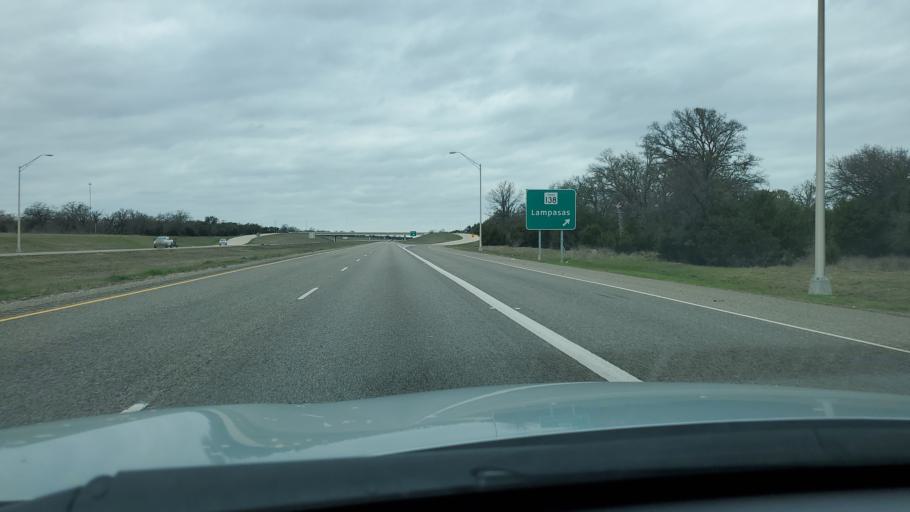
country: US
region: Texas
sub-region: Williamson County
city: Florence
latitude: 30.8509
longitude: -97.7899
